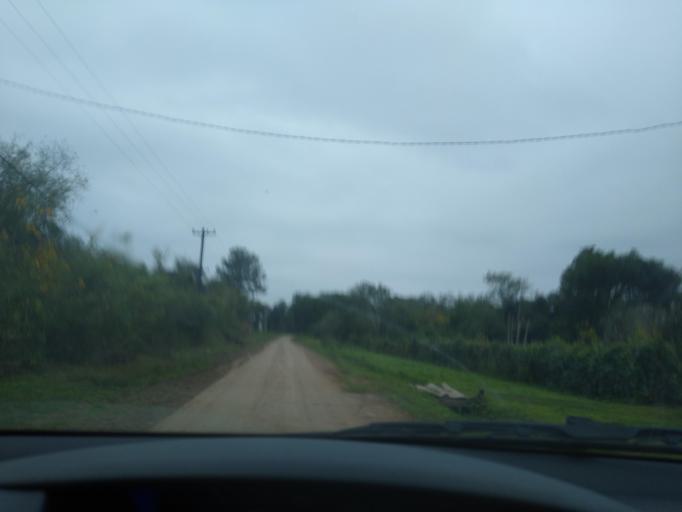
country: AR
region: Chaco
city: Colonia Benitez
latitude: -27.3322
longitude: -58.9588
